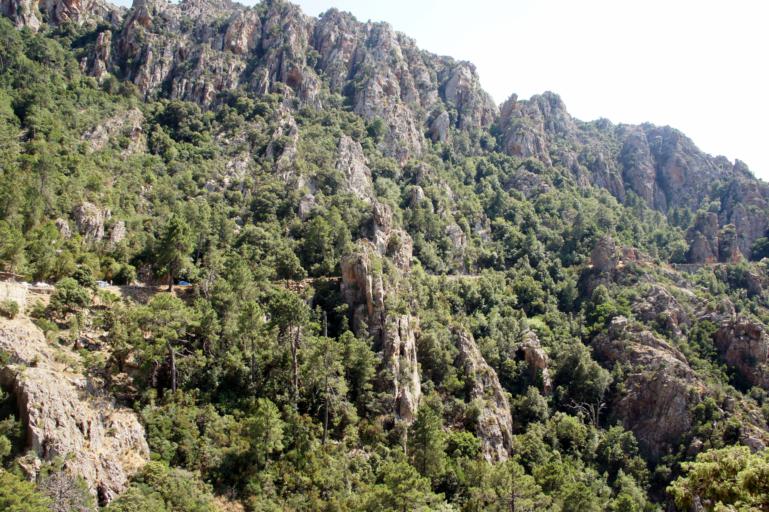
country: FR
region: Corsica
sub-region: Departement de la Corse-du-Sud
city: Cargese
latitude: 42.2491
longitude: 8.6605
